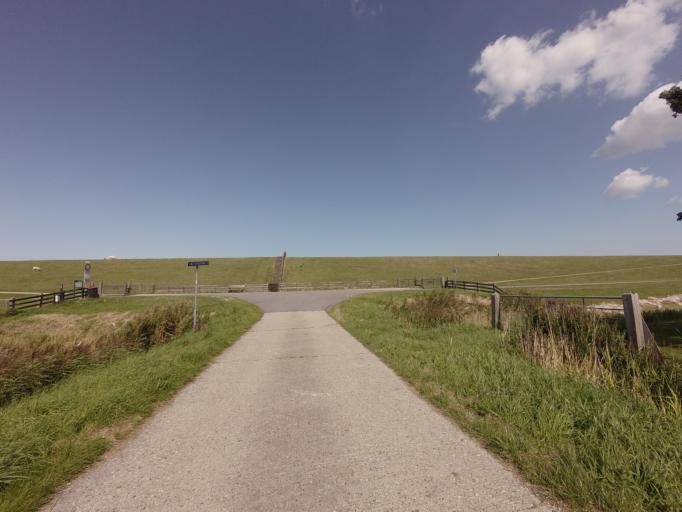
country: NL
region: Friesland
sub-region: Gemeente Ferwerderadiel
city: Hallum
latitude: 53.3237
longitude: 5.7220
